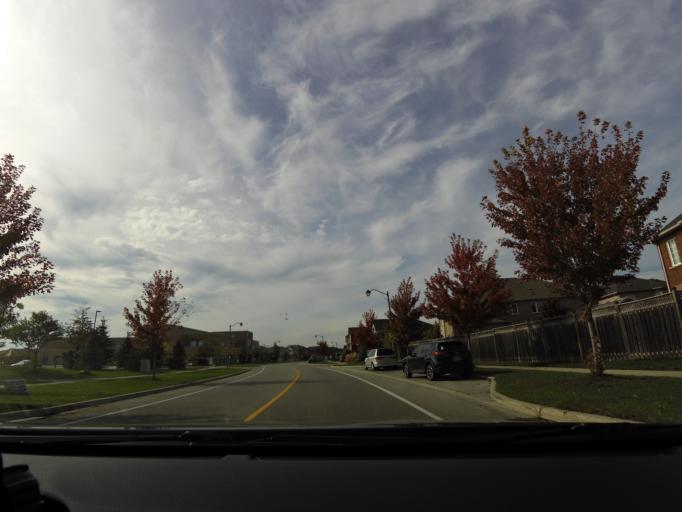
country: CA
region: Ontario
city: Burlington
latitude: 43.4094
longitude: -79.7930
